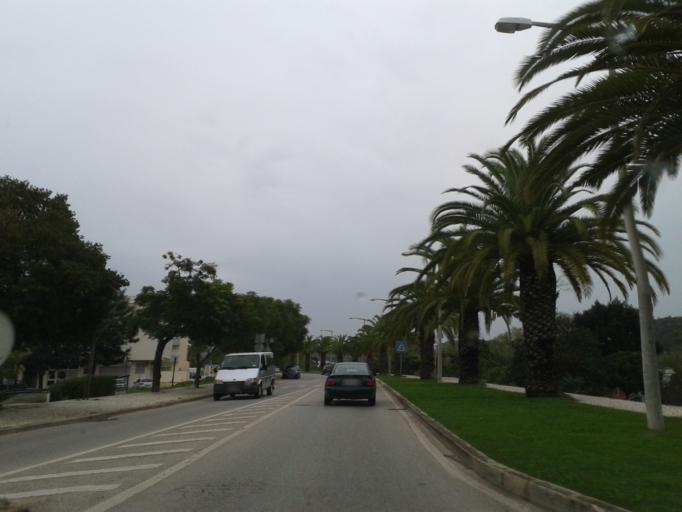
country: PT
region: Faro
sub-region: Silves
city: Silves
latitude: 37.1885
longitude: -8.4359
